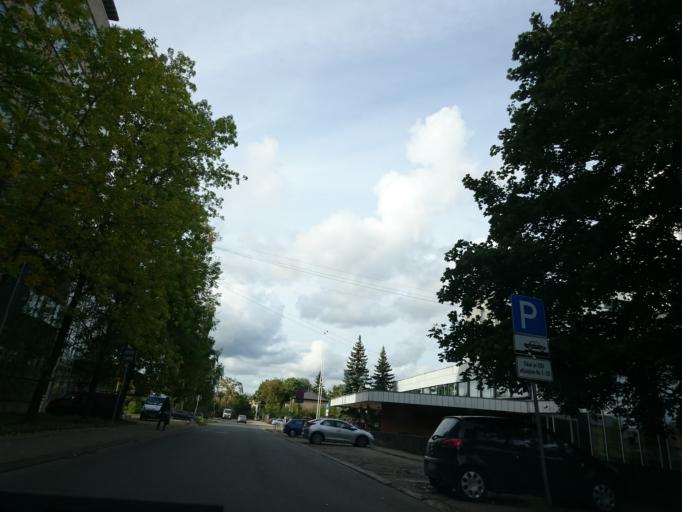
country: LV
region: Riga
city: Jaunciems
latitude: 56.9767
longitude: 24.1944
